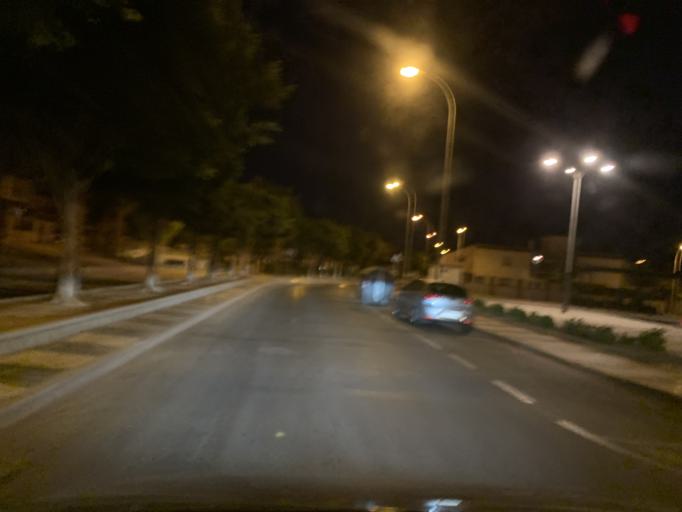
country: ES
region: Andalusia
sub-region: Provincia de Almeria
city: Roquetas de Mar
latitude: 36.7658
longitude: -2.6089
